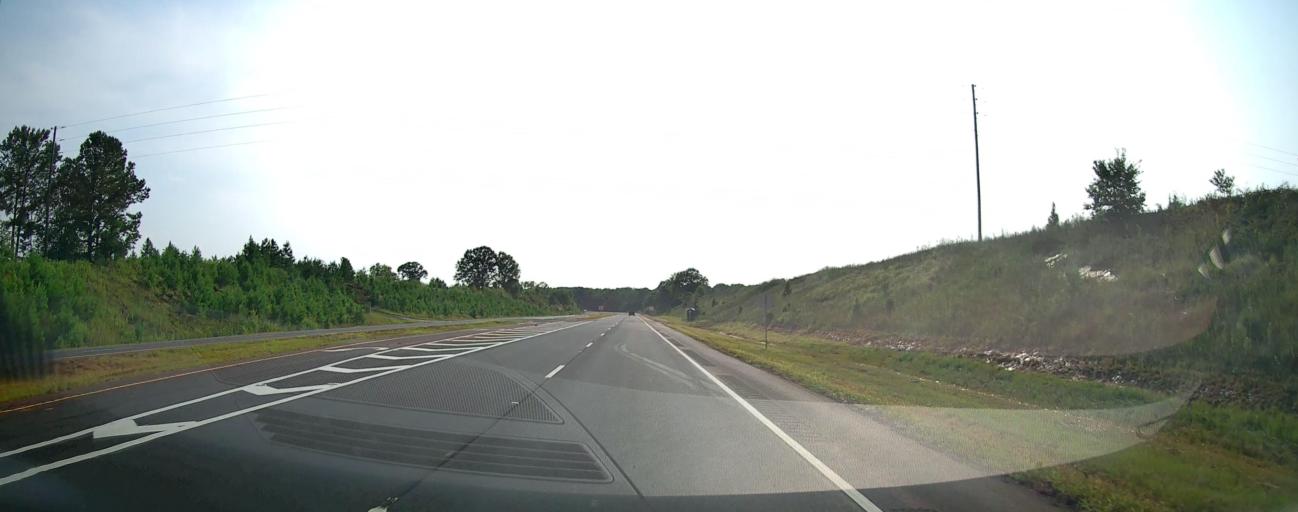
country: US
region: Georgia
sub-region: Peach County
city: Fort Valley
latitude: 32.5696
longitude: -83.9266
